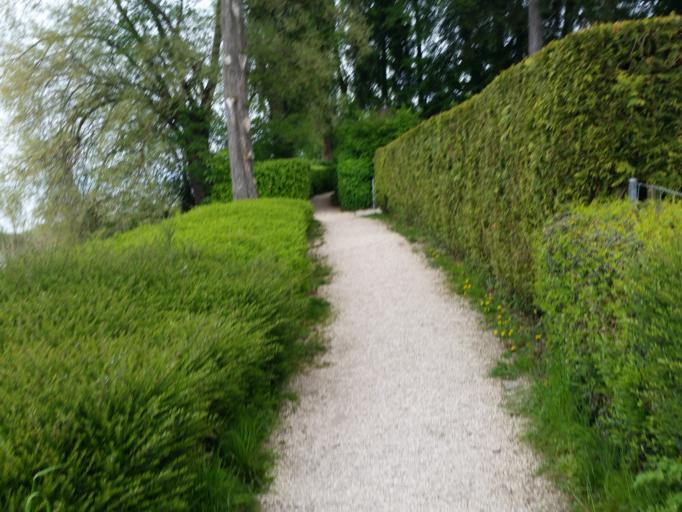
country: CH
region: Thurgau
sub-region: Arbon District
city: Uttwil
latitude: 47.5894
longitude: 9.3353
